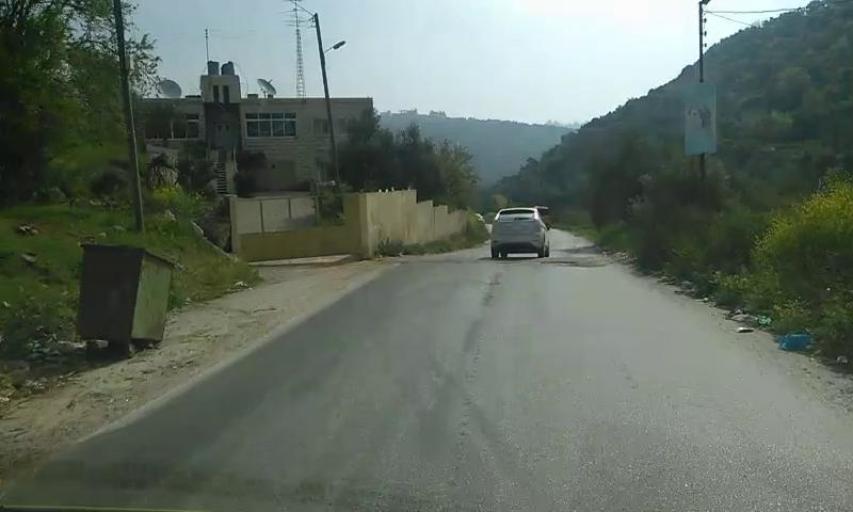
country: PS
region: West Bank
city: Dura al Qar`
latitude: 31.9563
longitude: 35.2313
